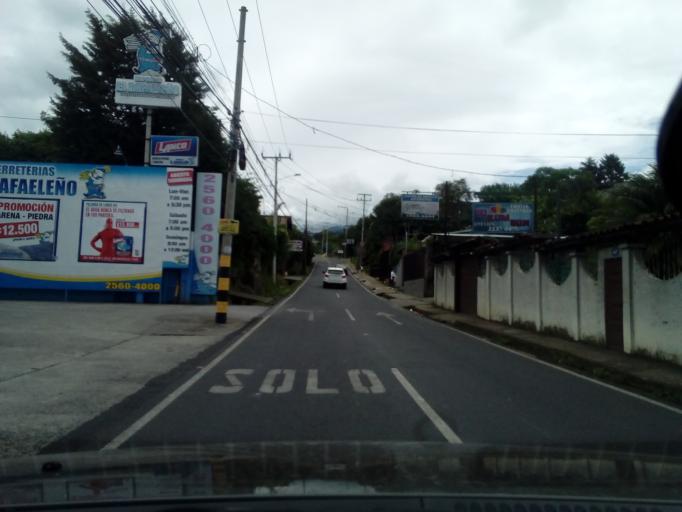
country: CR
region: Heredia
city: Mercedes
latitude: 10.0227
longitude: -84.1240
